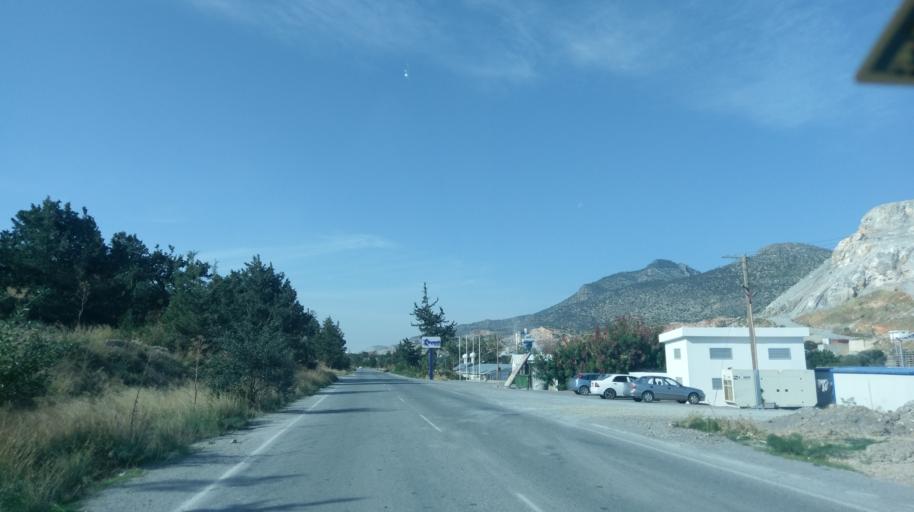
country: CY
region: Lefkosia
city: Nicosia
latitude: 35.2686
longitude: 33.4745
